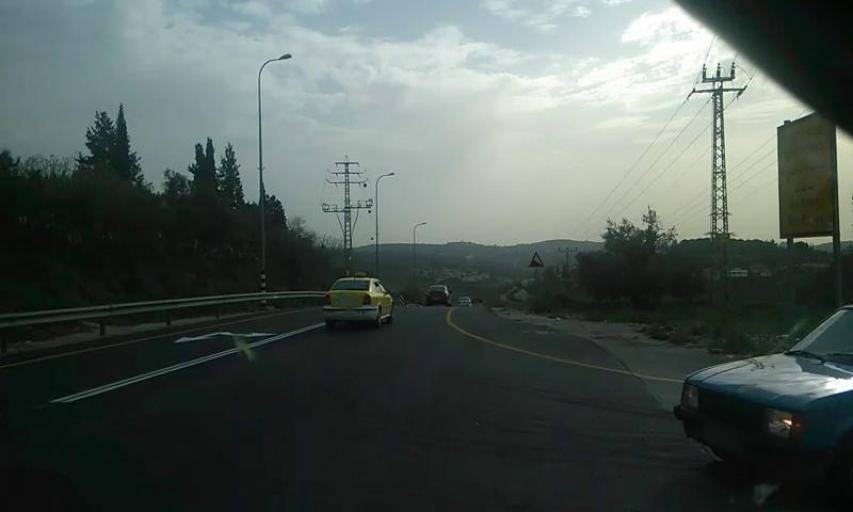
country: PS
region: West Bank
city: Jit
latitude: 32.2156
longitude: 35.1680
